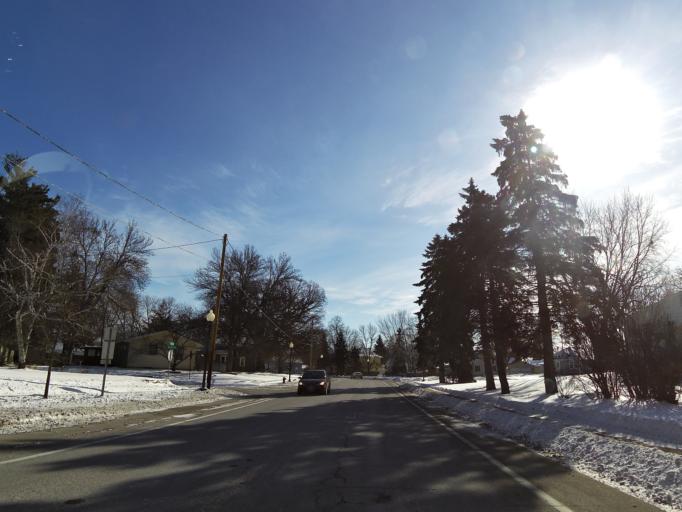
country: US
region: Minnesota
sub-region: Dakota County
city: Hastings
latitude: 44.7449
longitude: -92.8671
